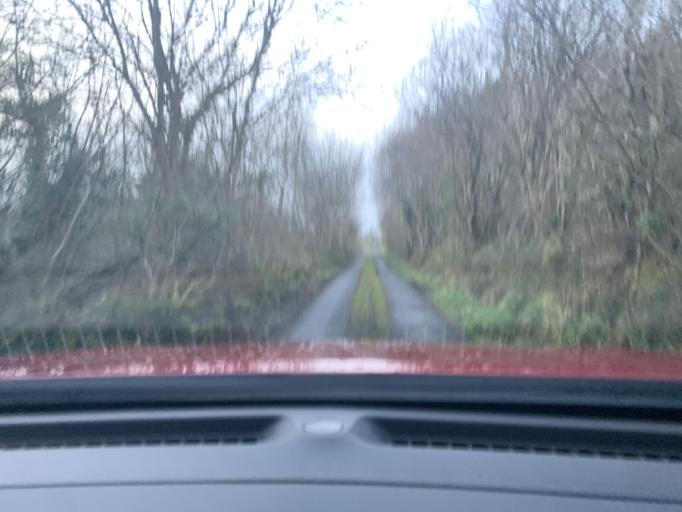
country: IE
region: Connaught
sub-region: Sligo
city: Ballymote
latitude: 53.9907
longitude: -8.4502
